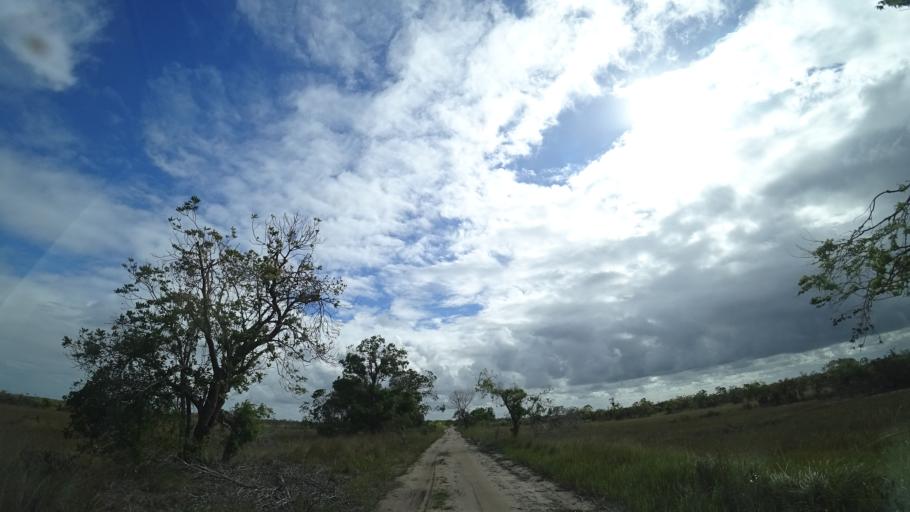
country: MZ
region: Sofala
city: Beira
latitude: -19.5792
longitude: 35.1744
